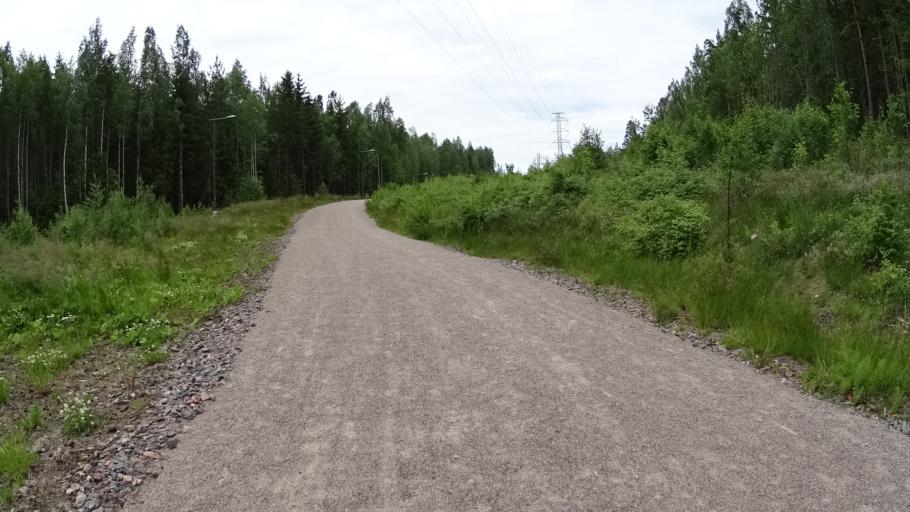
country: FI
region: Uusimaa
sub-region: Helsinki
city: Kauniainen
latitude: 60.1844
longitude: 24.7263
